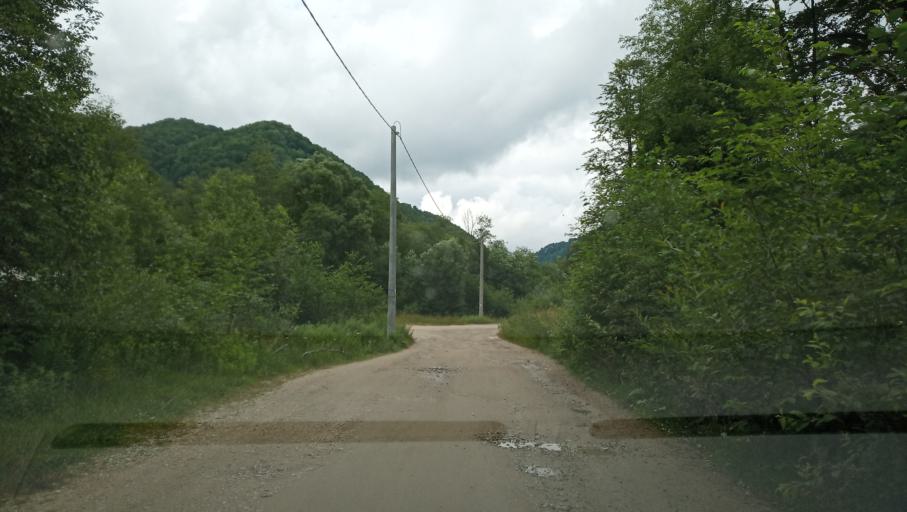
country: RO
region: Hunedoara
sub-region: Oras Petrila
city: Petrila
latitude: 45.4849
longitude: 23.4176
